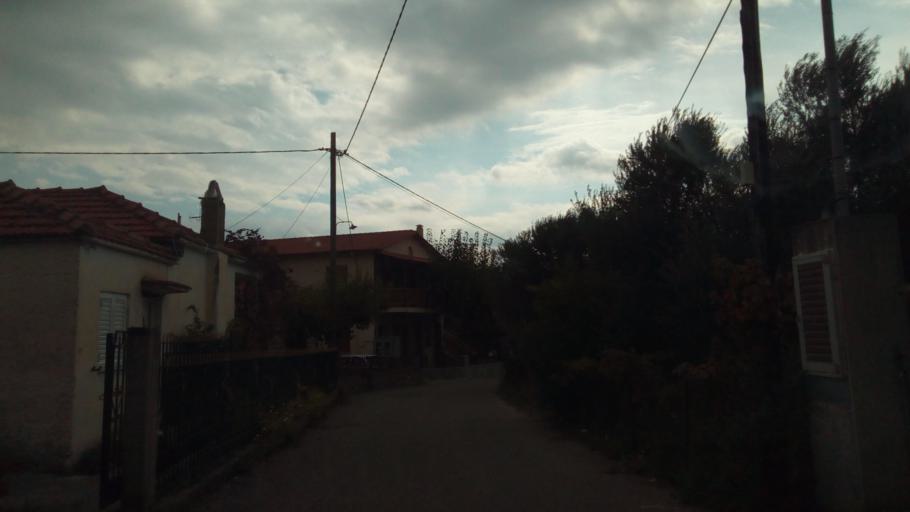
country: GR
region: West Greece
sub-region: Nomos Achaias
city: Kamarai
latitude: 38.3925
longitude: 22.0109
